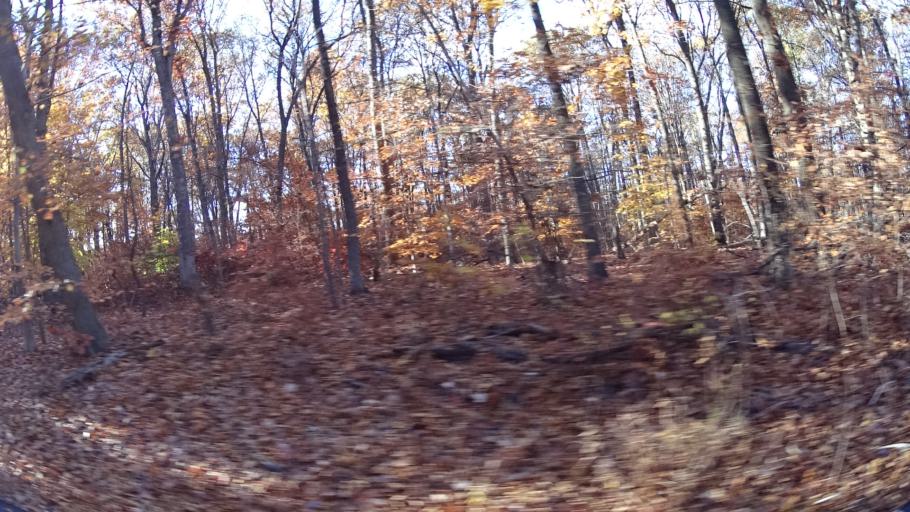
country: US
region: New Jersey
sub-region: Union County
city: Scotch Plains
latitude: 40.6665
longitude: -74.3977
